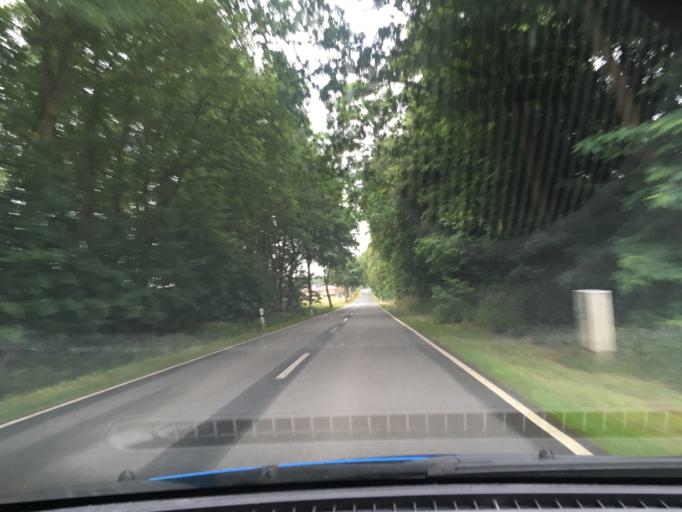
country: DE
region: Lower Saxony
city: Egestorf
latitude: 53.2018
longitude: 10.0673
